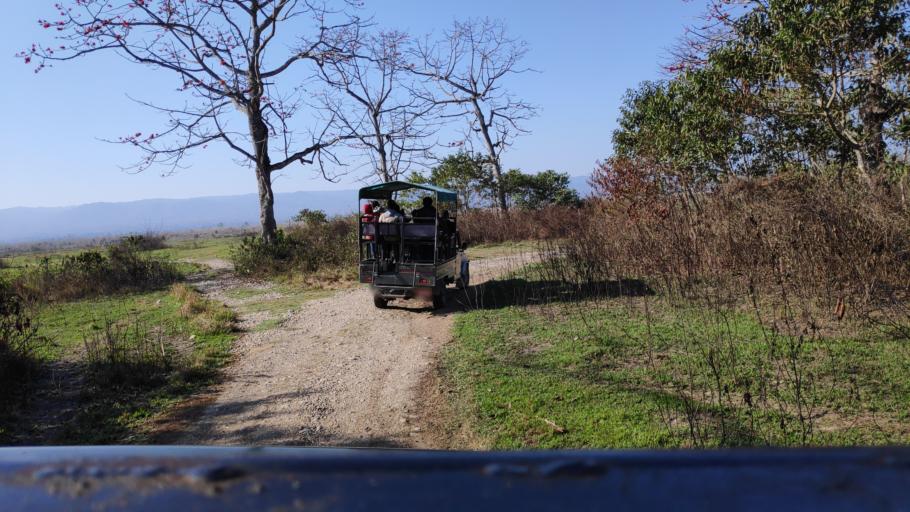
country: NP
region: Central Region
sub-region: Narayani Zone
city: Bharatpur
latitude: 27.5598
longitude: 84.5253
